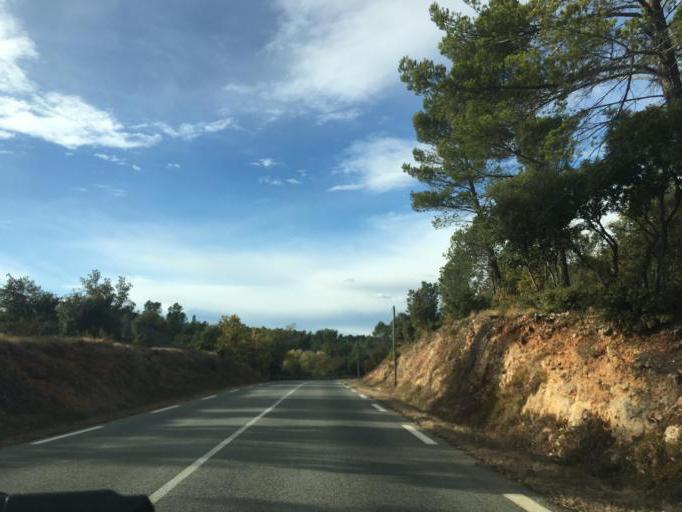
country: FR
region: Provence-Alpes-Cote d'Azur
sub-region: Departement du Var
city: Aups
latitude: 43.6015
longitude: 6.2384
